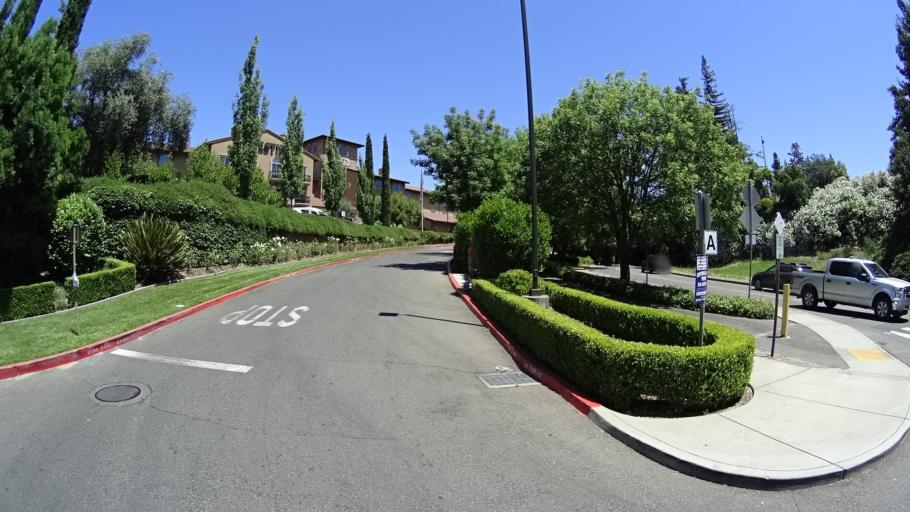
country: US
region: California
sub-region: Yolo County
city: West Sacramento
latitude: 38.5336
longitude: -121.5182
